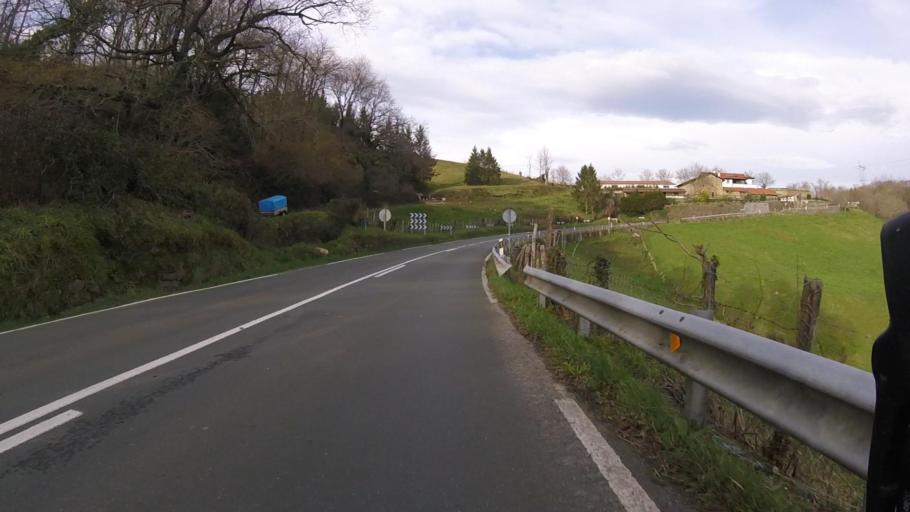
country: ES
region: Basque Country
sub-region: Provincia de Guipuzcoa
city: Lezo
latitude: 43.3024
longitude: -1.8526
